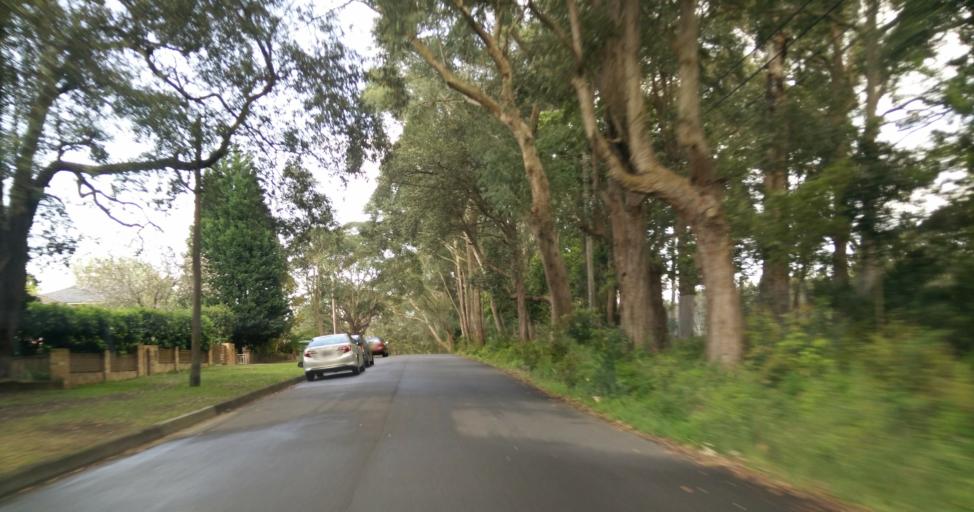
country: AU
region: New South Wales
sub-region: Ku-ring-gai
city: Killara
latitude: -33.7764
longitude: 151.1551
